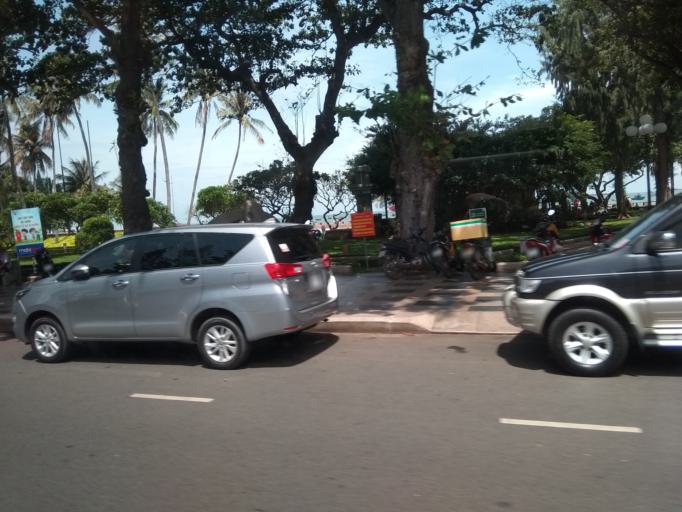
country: VN
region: Ba Ria-Vung Tau
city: Vung Tau
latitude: 10.3427
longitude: 107.0749
